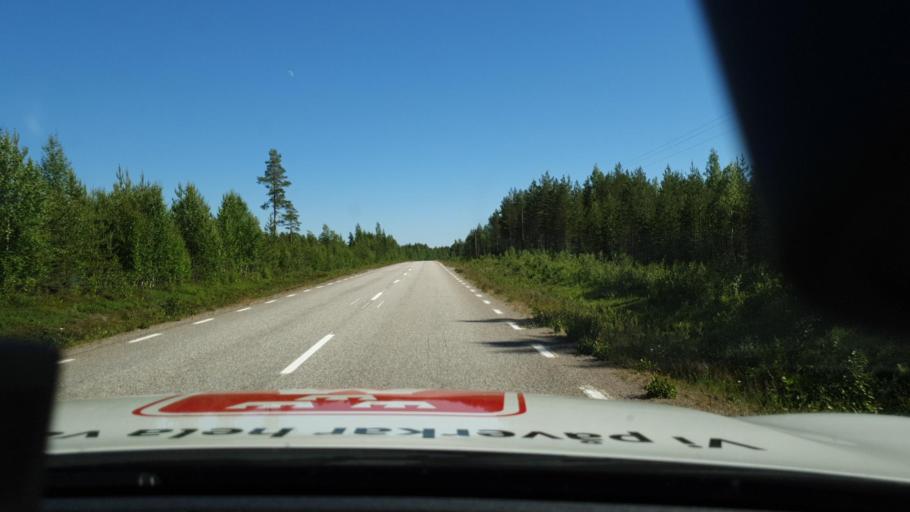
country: SE
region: Norrbotten
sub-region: Lulea Kommun
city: Ranea
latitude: 65.9804
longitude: 22.3655
